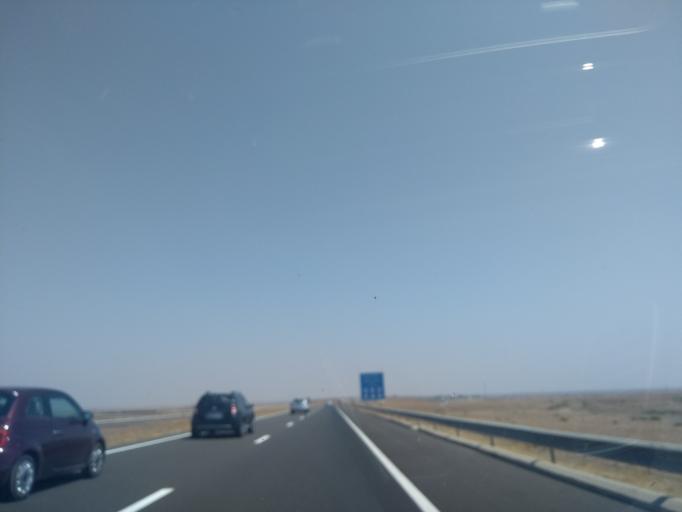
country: MA
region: Marrakech-Tensift-Al Haouz
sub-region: Kelaa-Des-Sraghna
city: Sidi Bou Othmane
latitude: 31.9055
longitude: -8.0256
